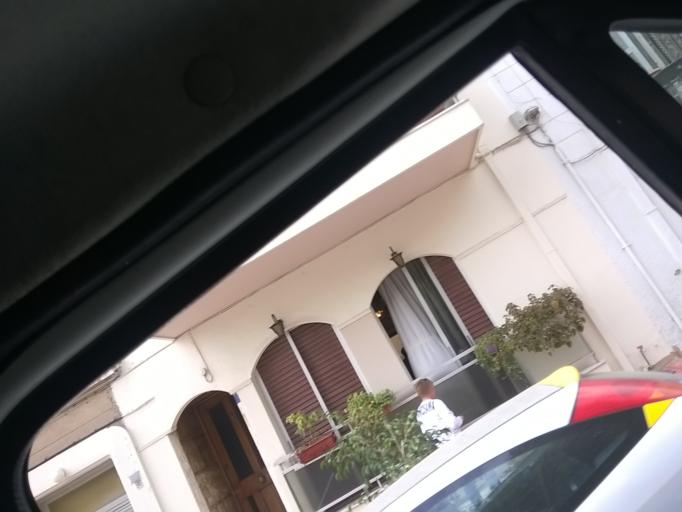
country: GR
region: Attica
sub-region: Nomos Attikis
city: Piraeus
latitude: 37.9377
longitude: 23.6546
